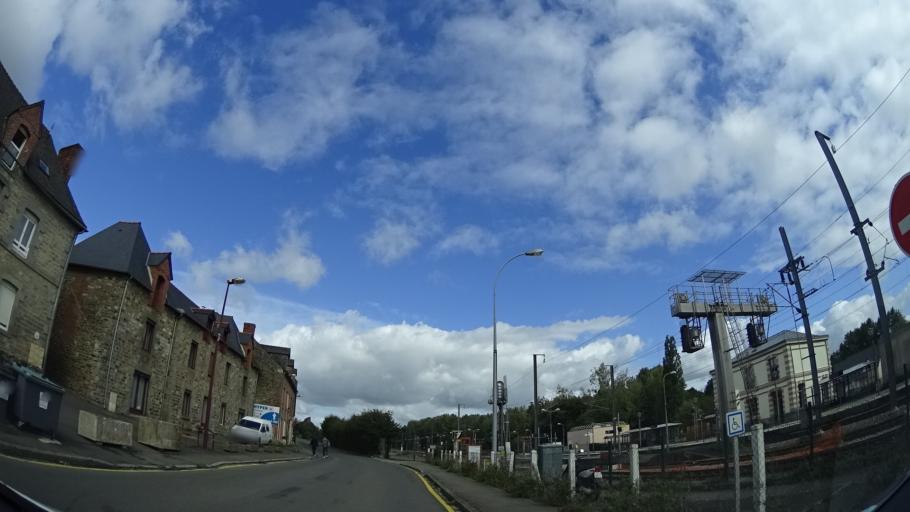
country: FR
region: Brittany
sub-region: Departement d'Ille-et-Vilaine
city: Montreuil-sur-Ille
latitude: 48.3068
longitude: -1.6745
